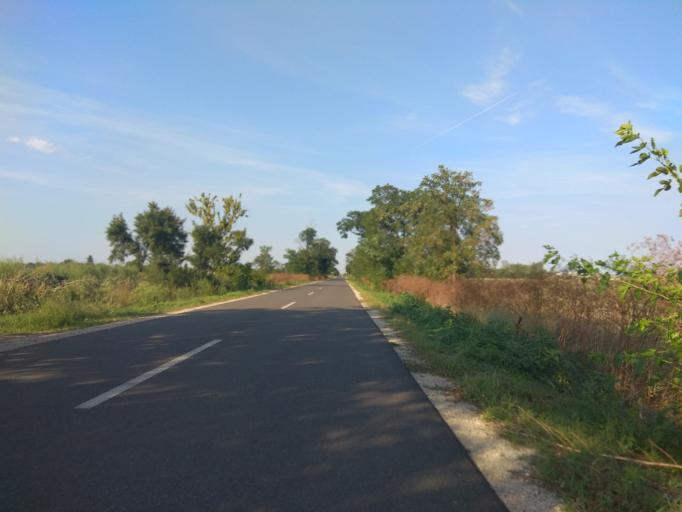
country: HU
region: Borsod-Abauj-Zemplen
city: Emod
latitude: 47.8816
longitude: 20.7662
